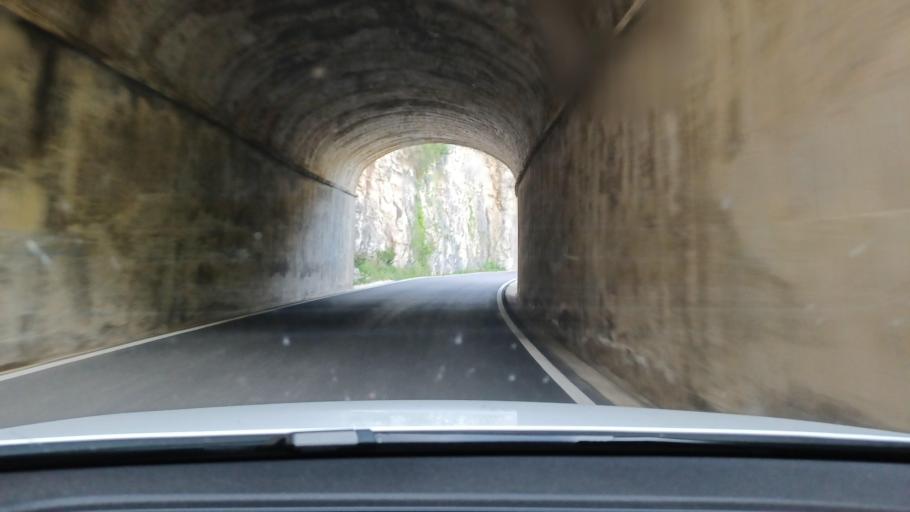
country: ES
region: Valencia
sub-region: Provincia de Castello
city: Rosell
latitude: 40.6702
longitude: 0.2376
